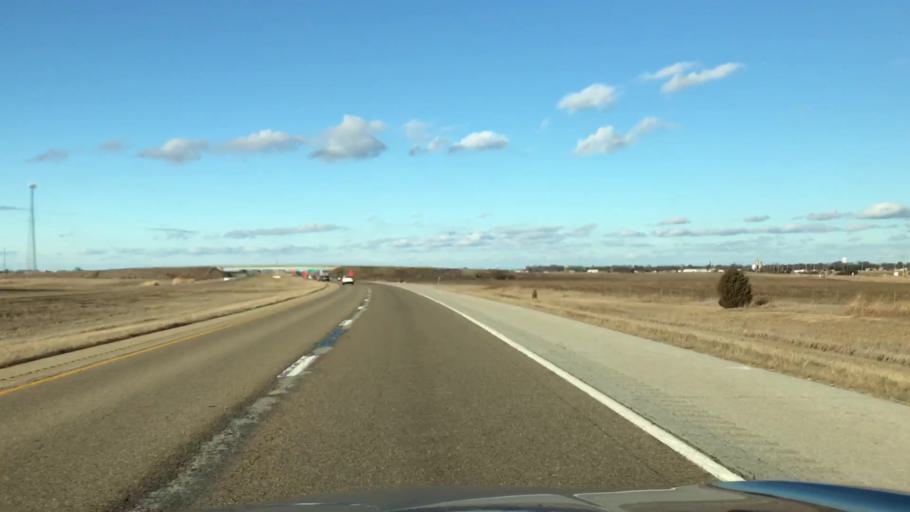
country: US
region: Illinois
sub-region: McLean County
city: Chenoa
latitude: 40.7219
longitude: -88.7371
